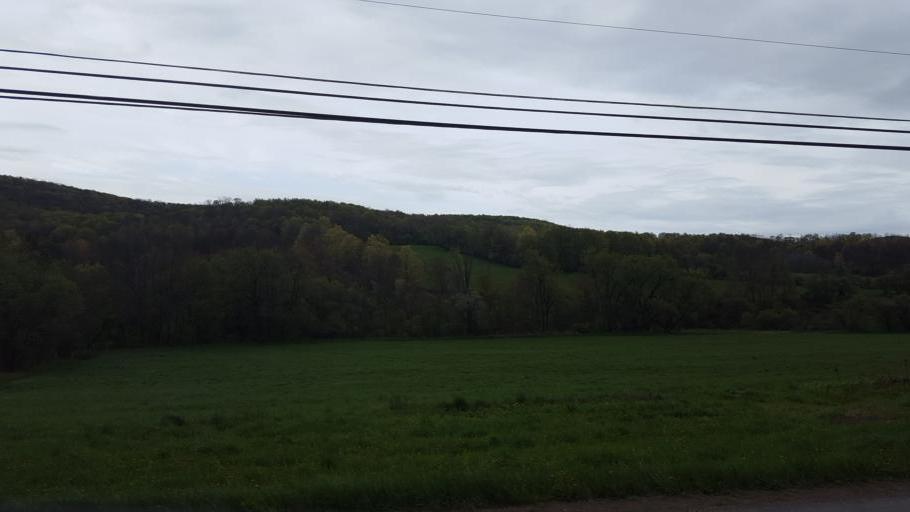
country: US
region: Pennsylvania
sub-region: Tioga County
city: Westfield
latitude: 41.9460
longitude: -77.6826
